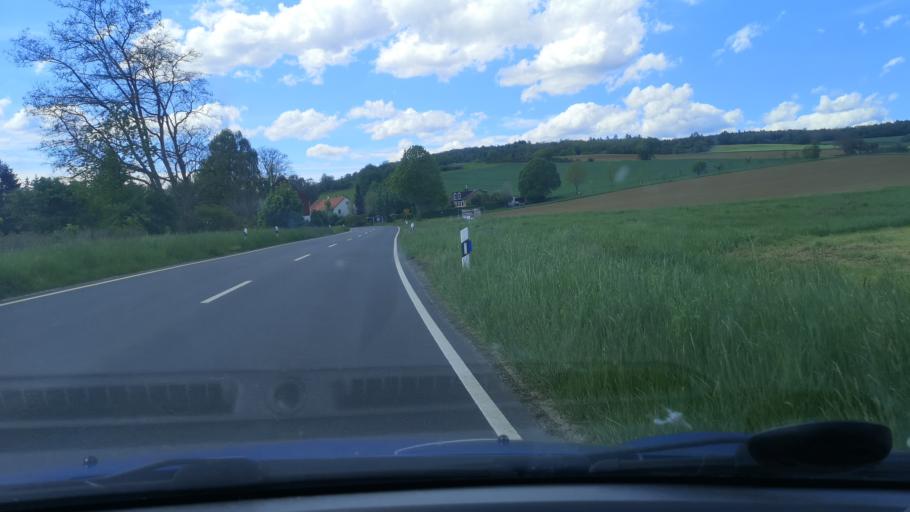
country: DE
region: Lower Saxony
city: Adelebsen
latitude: 51.5889
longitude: 9.8149
